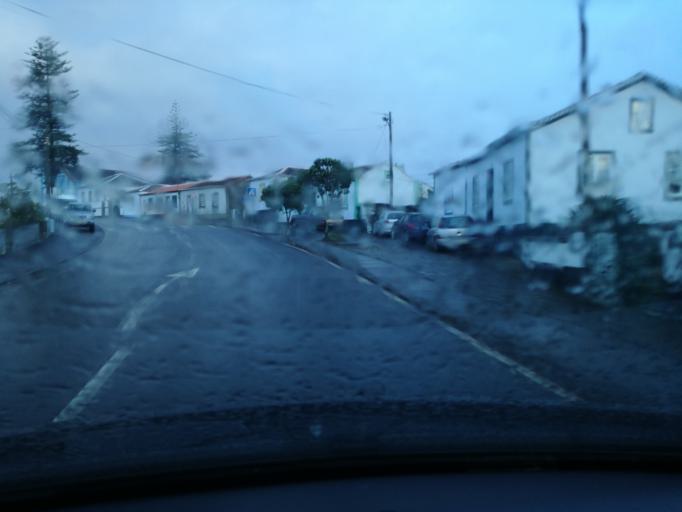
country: PT
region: Azores
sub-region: Praia da Vitoria
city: Praia da Vitoria
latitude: 38.7077
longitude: -27.0597
